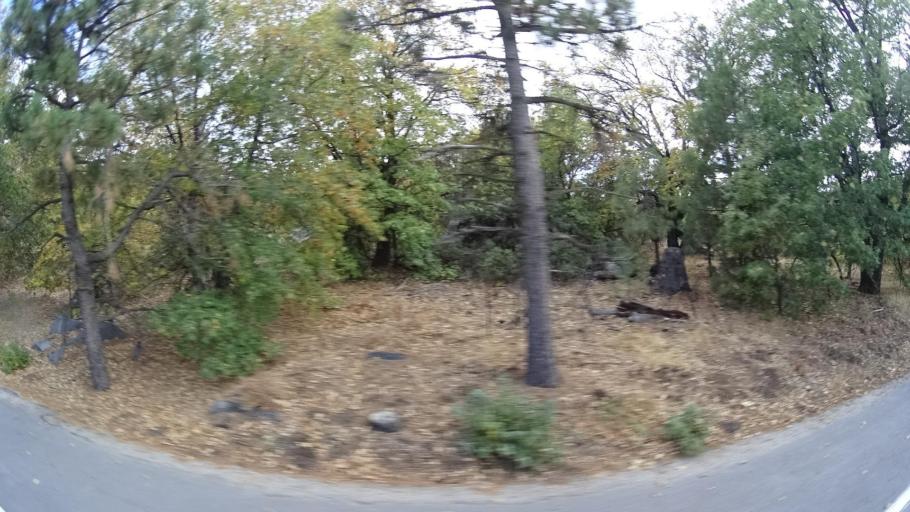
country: US
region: California
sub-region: San Diego County
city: Pine Valley
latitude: 32.8483
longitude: -116.4281
